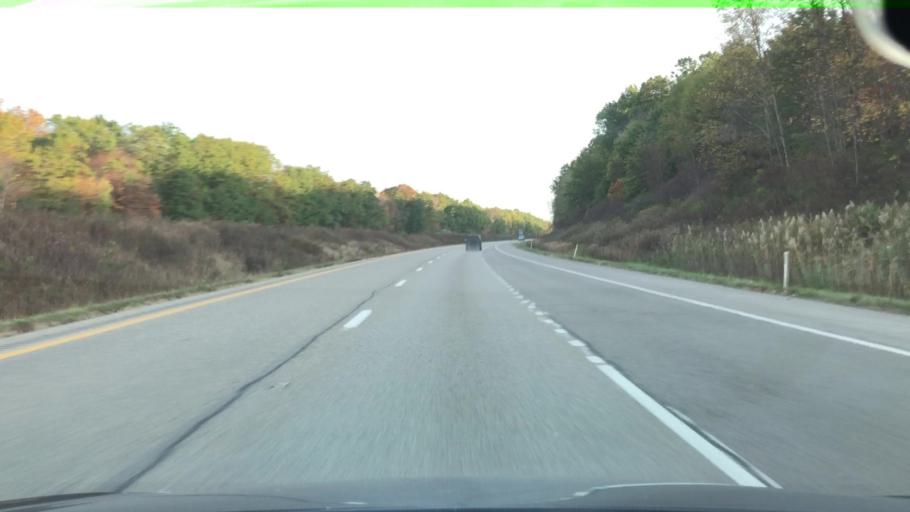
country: US
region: Pennsylvania
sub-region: Mercer County
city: Mercer
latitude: 41.2670
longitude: -80.1660
